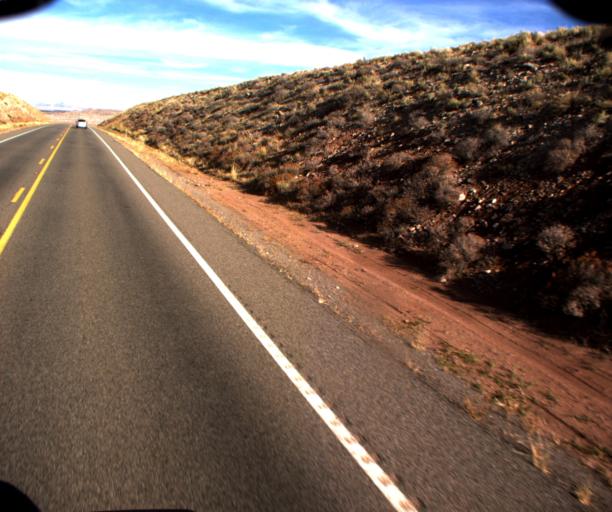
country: US
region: New Mexico
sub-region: San Juan County
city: Shiprock
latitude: 36.9279
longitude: -109.1652
